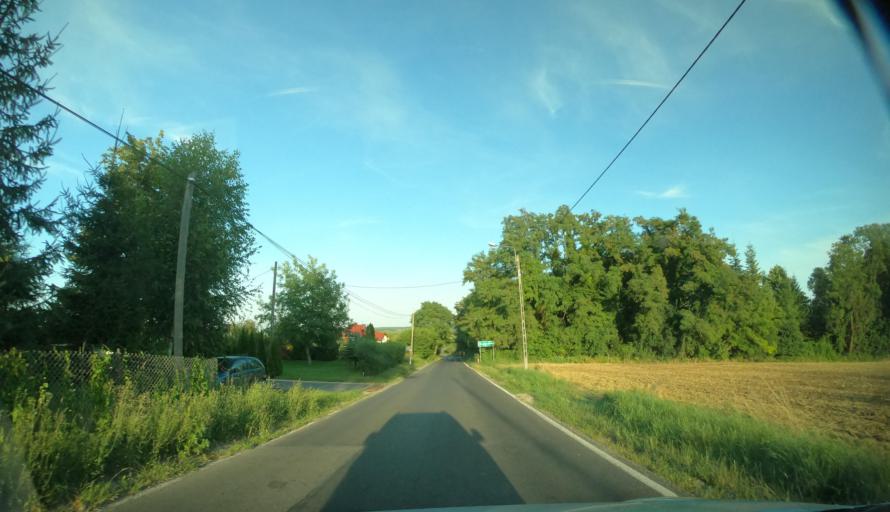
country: PL
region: Kujawsko-Pomorskie
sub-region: Bydgoszcz
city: Fordon
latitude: 53.2081
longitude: 18.1739
